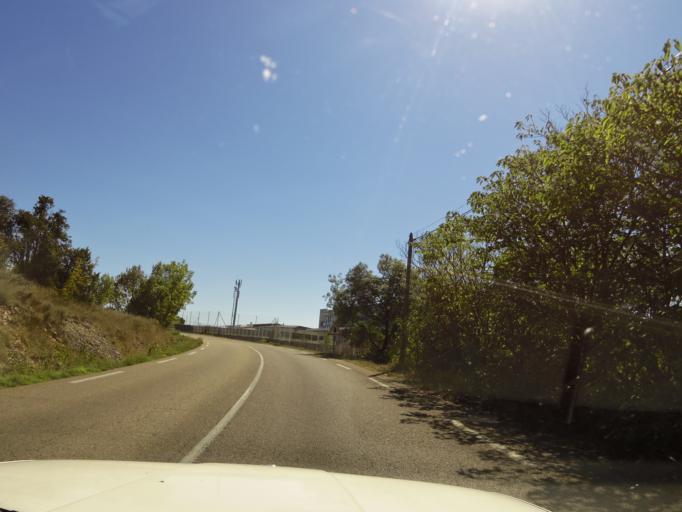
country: FR
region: Languedoc-Roussillon
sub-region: Departement du Gard
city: Saint-Hilaire-de-Brethmas
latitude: 44.0697
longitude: 4.1166
